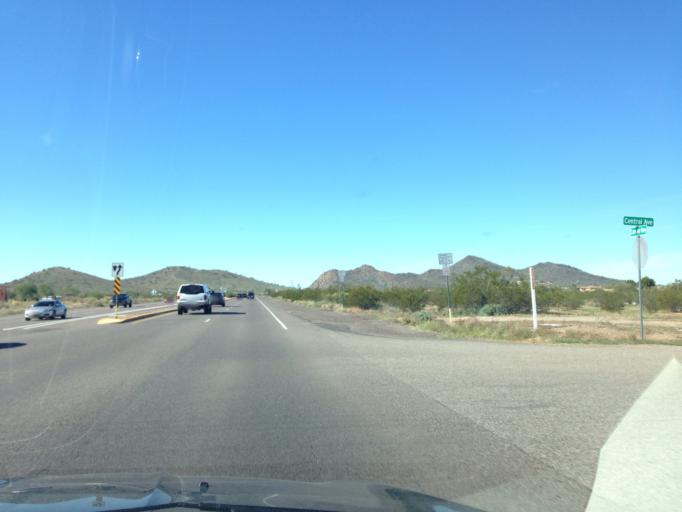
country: US
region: Arizona
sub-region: Maricopa County
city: Anthem
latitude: 33.7992
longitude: -112.0738
